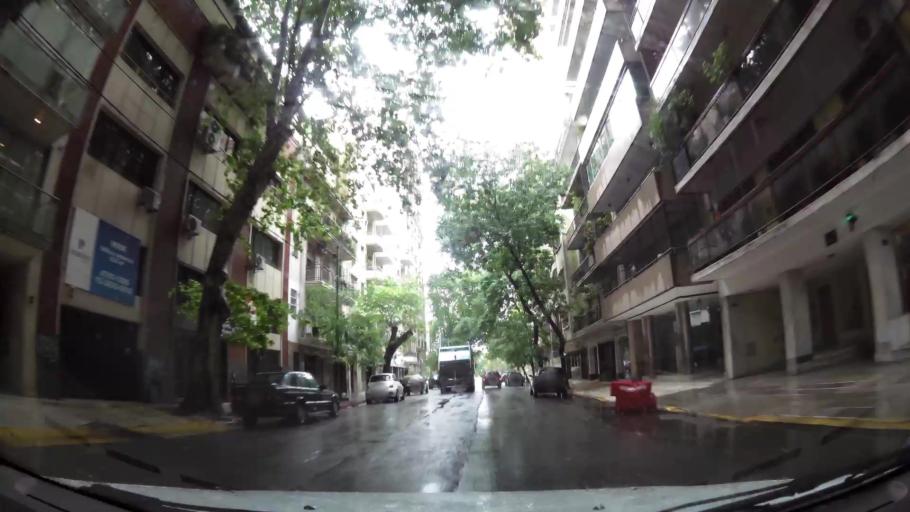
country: AR
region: Buenos Aires F.D.
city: Colegiales
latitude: -34.5732
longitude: -58.4211
